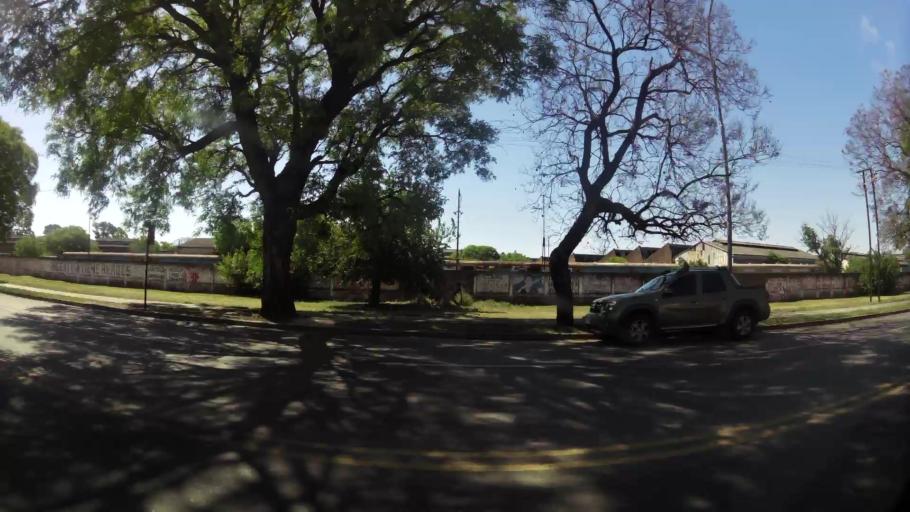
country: AR
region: Cordoba
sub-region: Departamento de Capital
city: Cordoba
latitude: -31.3973
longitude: -64.1633
